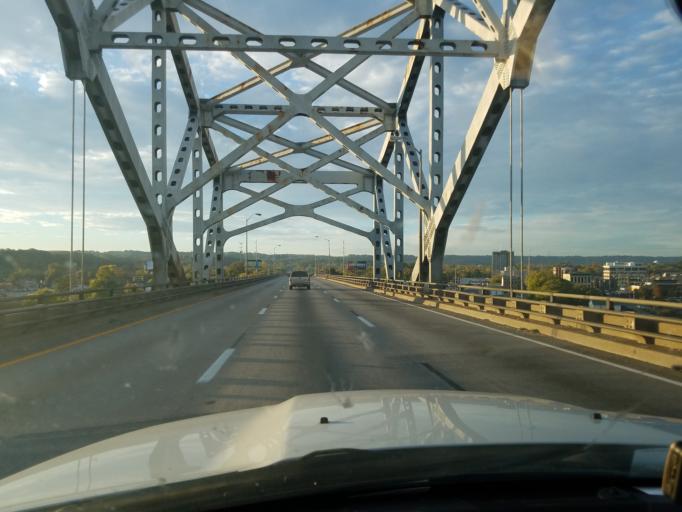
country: US
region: Indiana
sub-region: Floyd County
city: New Albany
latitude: 38.2798
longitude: -85.8234
